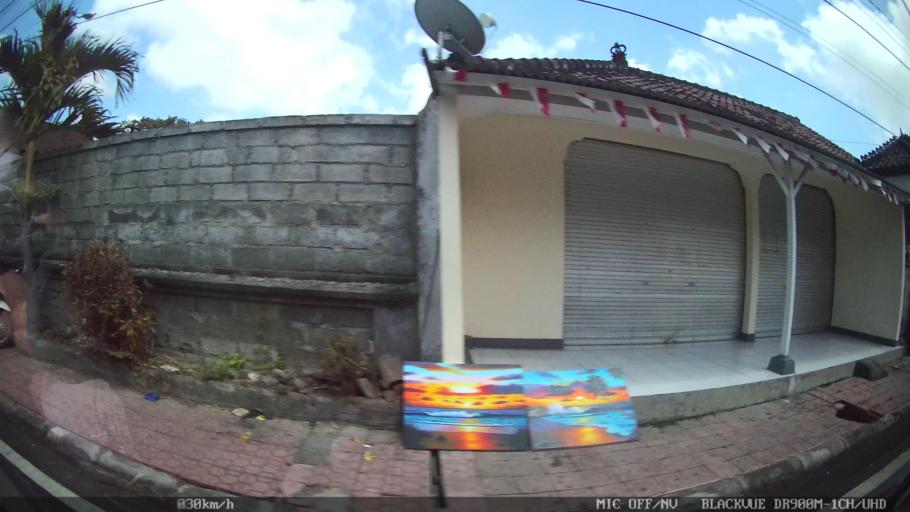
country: ID
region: Bali
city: Banjar Pasekan
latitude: -8.5973
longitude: 115.2804
